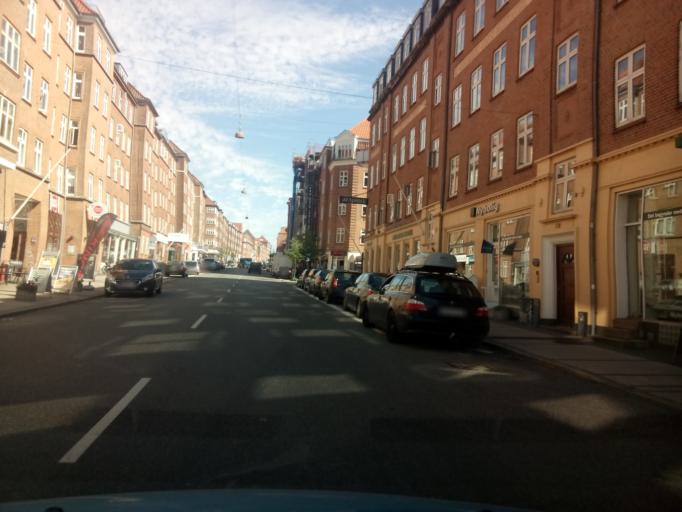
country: DK
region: Central Jutland
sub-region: Arhus Kommune
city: Arhus
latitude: 56.1702
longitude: 10.2162
